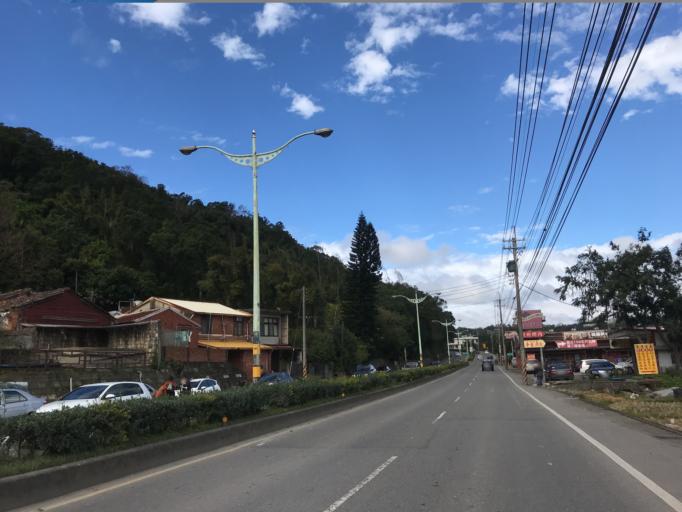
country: TW
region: Taiwan
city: Daxi
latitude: 24.8358
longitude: 121.2461
